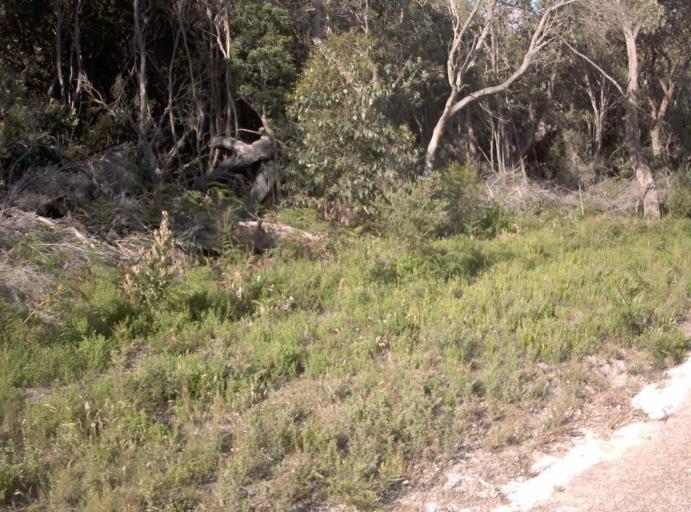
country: AU
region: Victoria
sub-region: East Gippsland
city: Lakes Entrance
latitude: -37.7985
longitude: 148.5807
